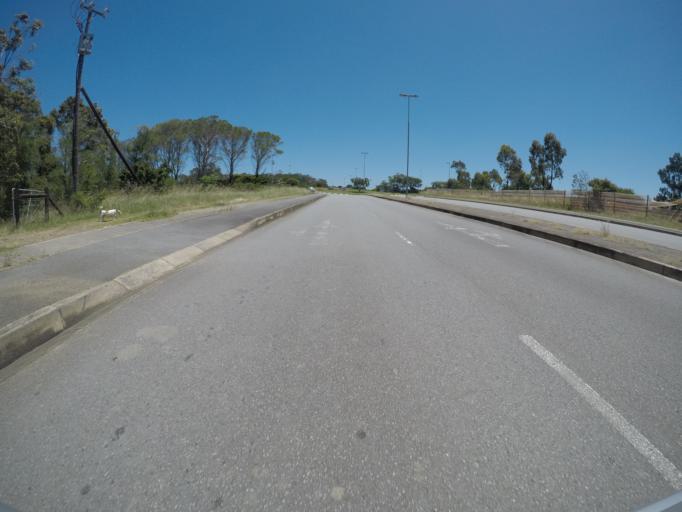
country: ZA
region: Eastern Cape
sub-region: Buffalo City Metropolitan Municipality
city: East London
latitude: -32.9494
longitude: 27.9410
